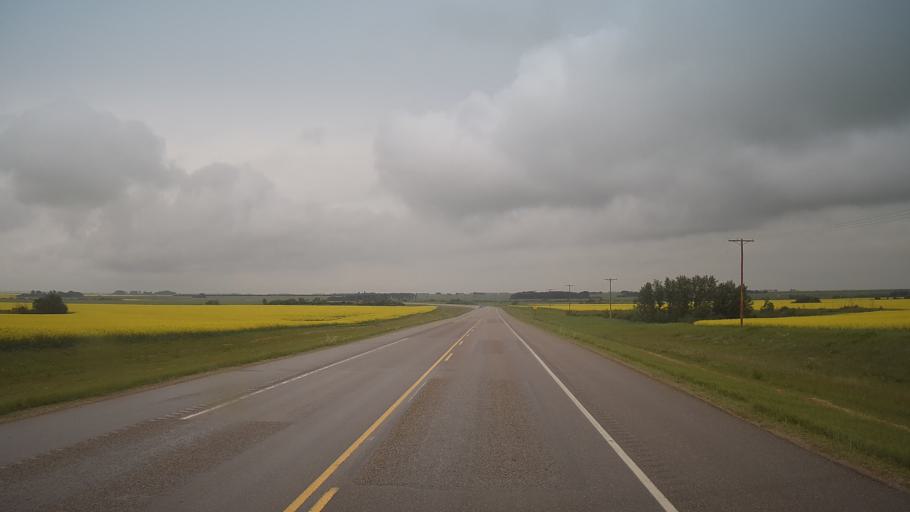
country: CA
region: Saskatchewan
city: Wilkie
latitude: 52.4313
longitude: -108.9208
